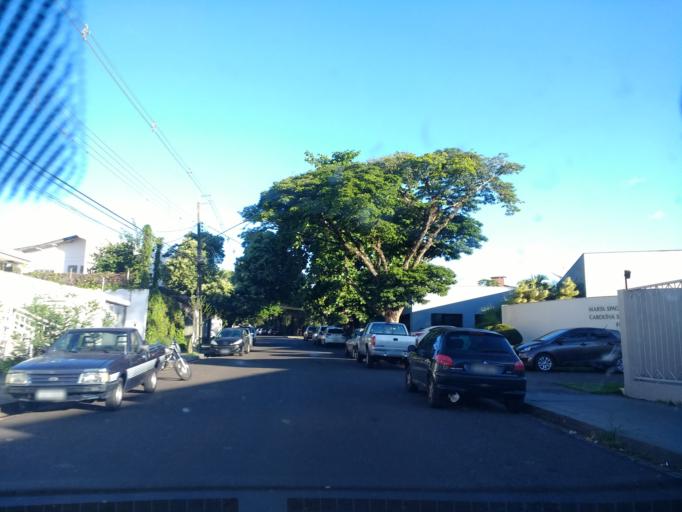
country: BR
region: Parana
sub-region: Londrina
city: Londrina
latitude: -23.3260
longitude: -51.1623
